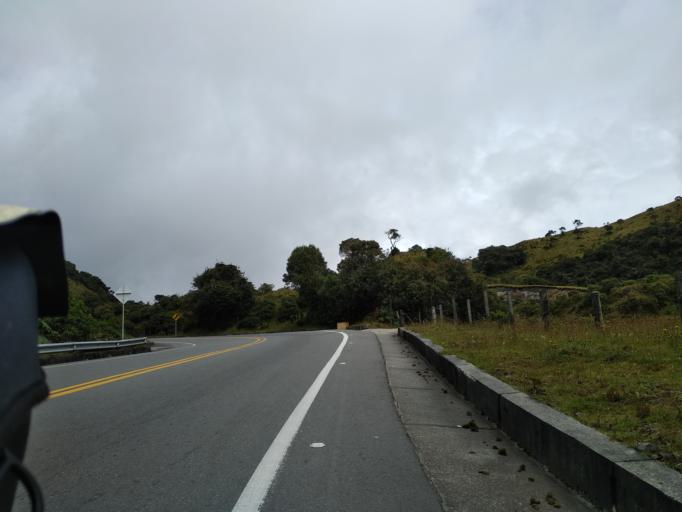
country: CO
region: Tolima
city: Herveo
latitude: 5.0722
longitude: -75.2853
